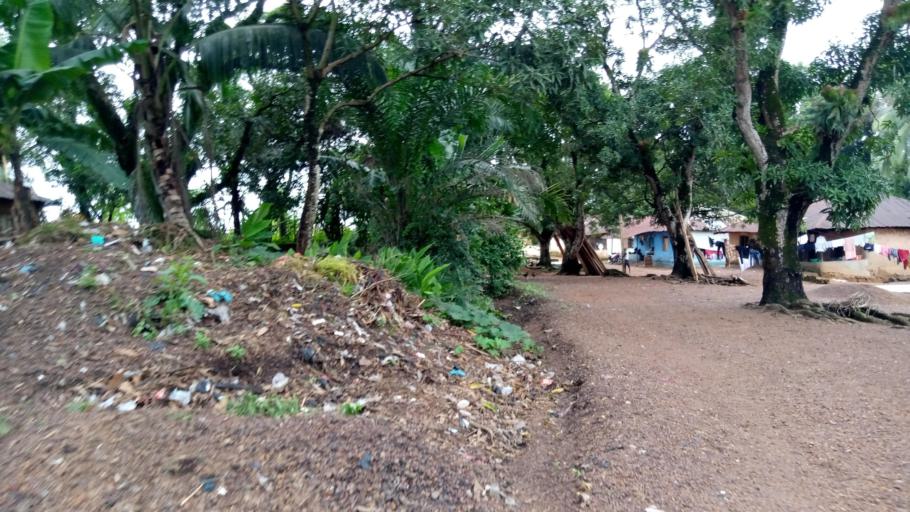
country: SL
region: Southern Province
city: Moyamba
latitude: 8.1580
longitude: -12.4331
